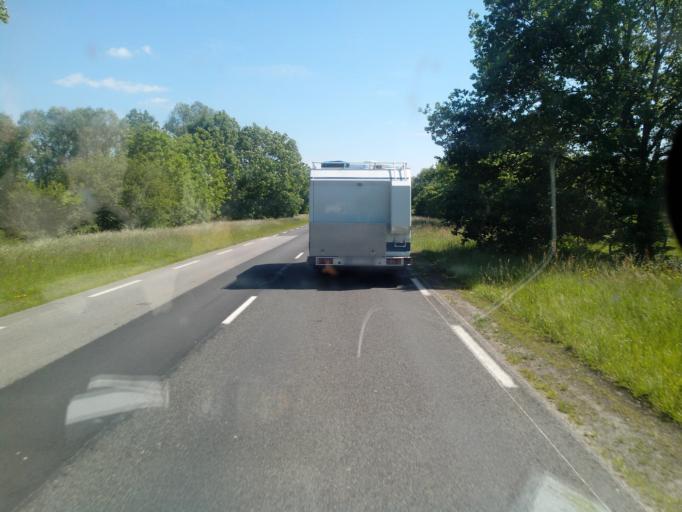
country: FR
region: Haute-Normandie
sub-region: Departement de l'Eure
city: Toutainville
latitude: 49.4077
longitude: 0.4250
